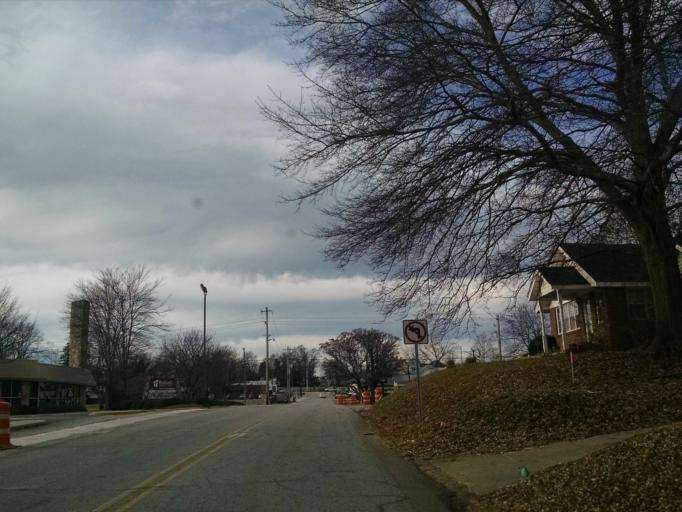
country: US
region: Georgia
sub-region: Gwinnett County
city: Buford
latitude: 34.1152
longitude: -84.0079
